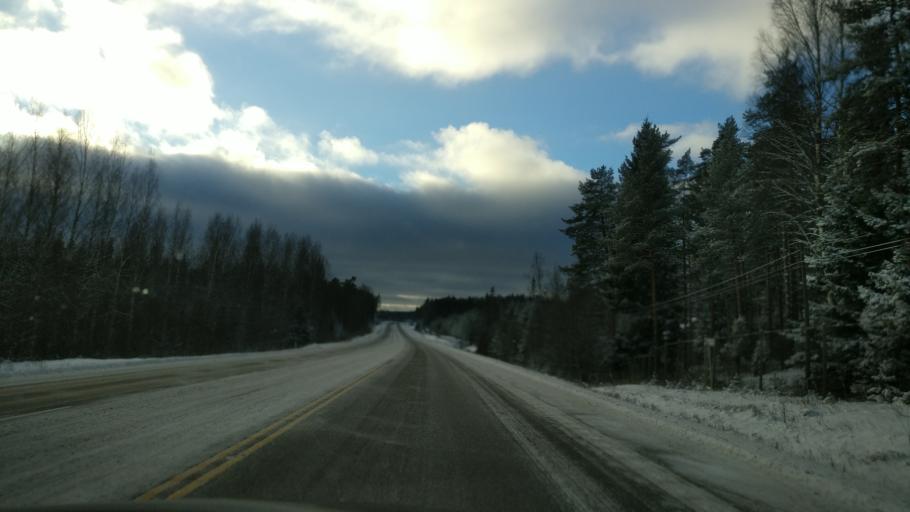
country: FI
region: Paijanne Tavastia
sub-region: Lahti
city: Heinola
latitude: 61.3433
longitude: 26.1957
